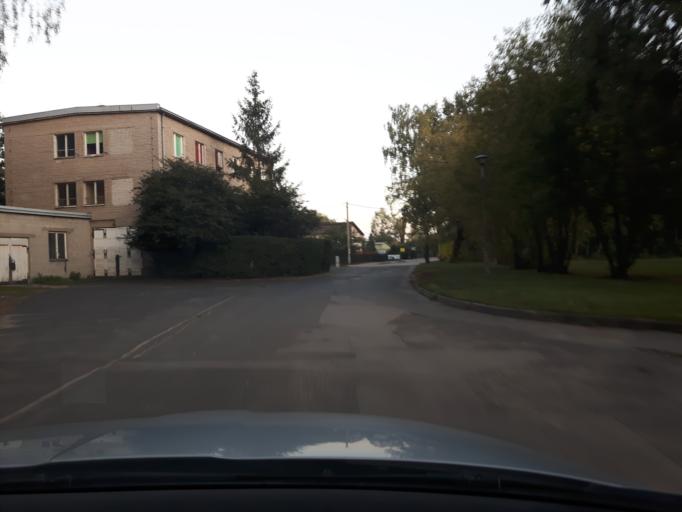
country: PL
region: Masovian Voivodeship
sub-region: Powiat wolominski
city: Kobylka
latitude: 52.3463
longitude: 21.1828
